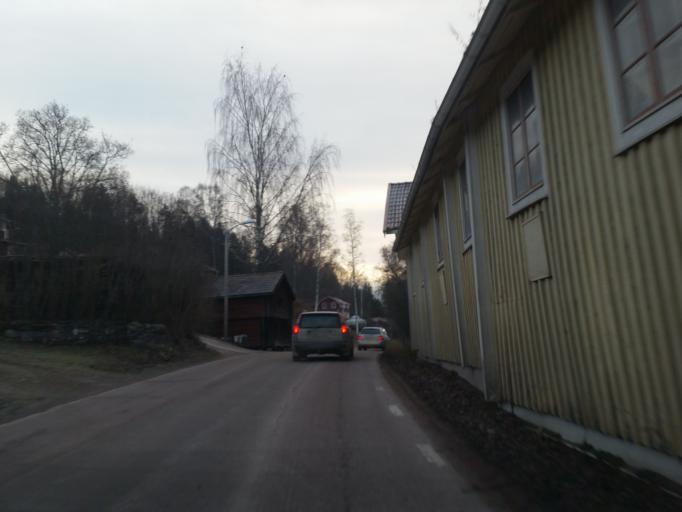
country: SE
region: Dalarna
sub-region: Leksand Municipality
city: Leksand
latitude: 60.7293
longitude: 15.0296
